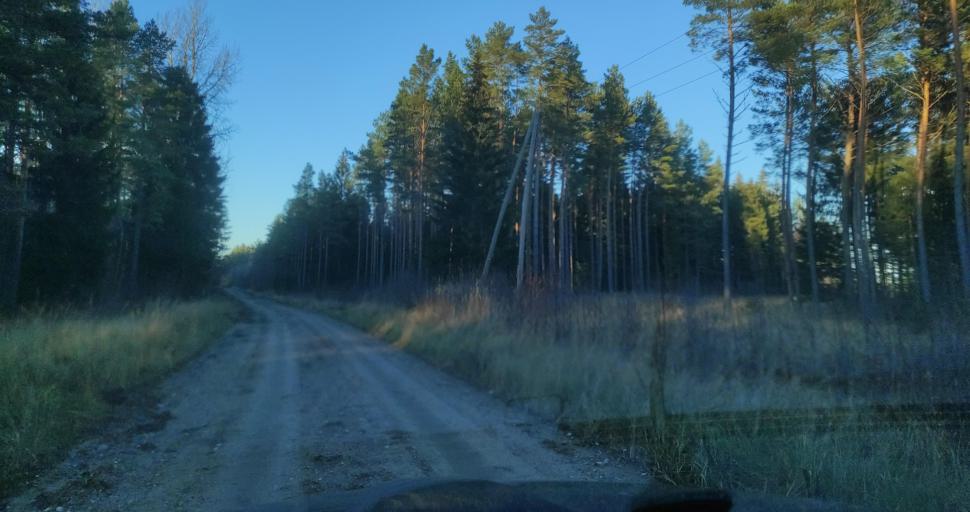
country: LV
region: Dundaga
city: Dundaga
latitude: 57.3787
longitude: 22.0821
